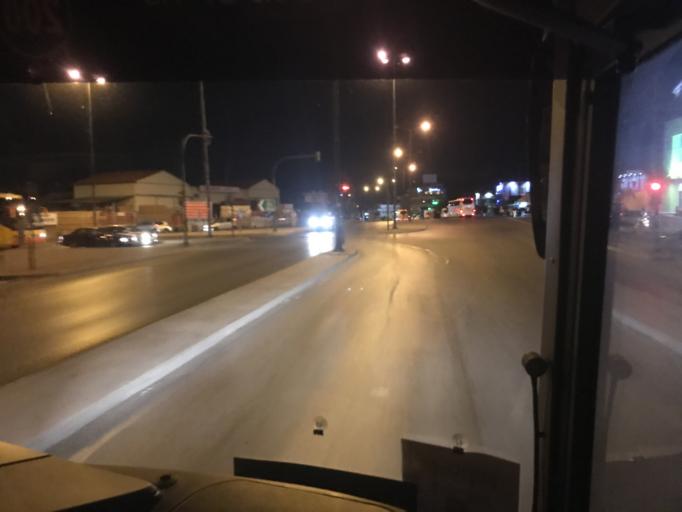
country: GR
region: Crete
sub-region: Nomos Irakleiou
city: Nea Alikarnassos
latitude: 35.3333
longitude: 25.1587
